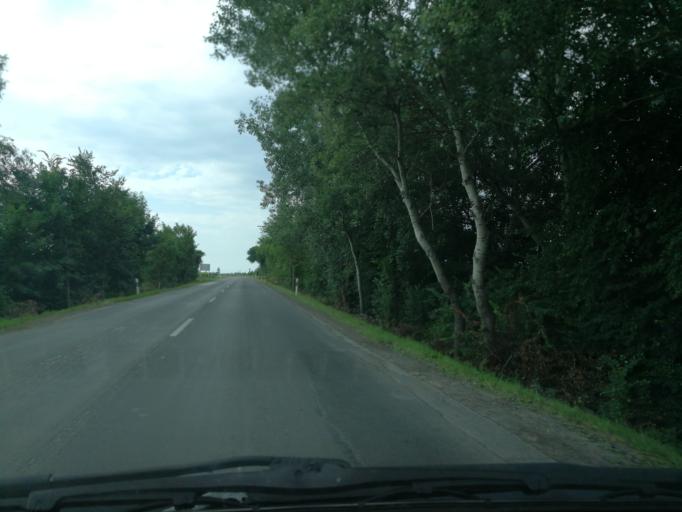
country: HU
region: Bacs-Kiskun
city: Dusnok
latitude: 46.3573
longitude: 18.9645
